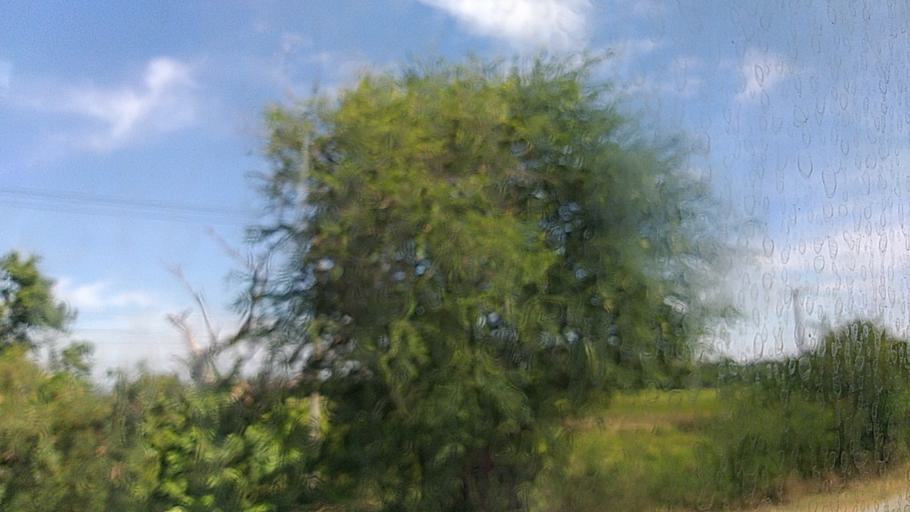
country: TH
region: Khon Kaen
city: Khon Kaen
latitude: 16.4072
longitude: 102.8894
